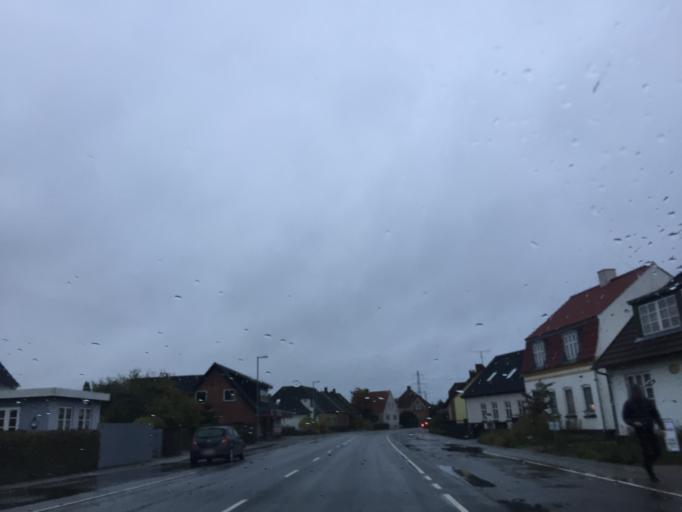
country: DK
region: Zealand
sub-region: Ringsted Kommune
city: Ringsted
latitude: 55.4580
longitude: 11.7896
